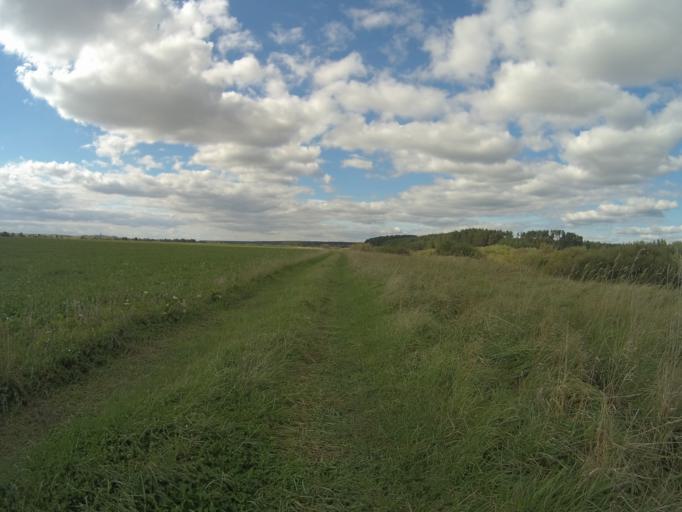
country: RU
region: Vladimir
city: Orgtrud
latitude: 56.3136
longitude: 40.6902
